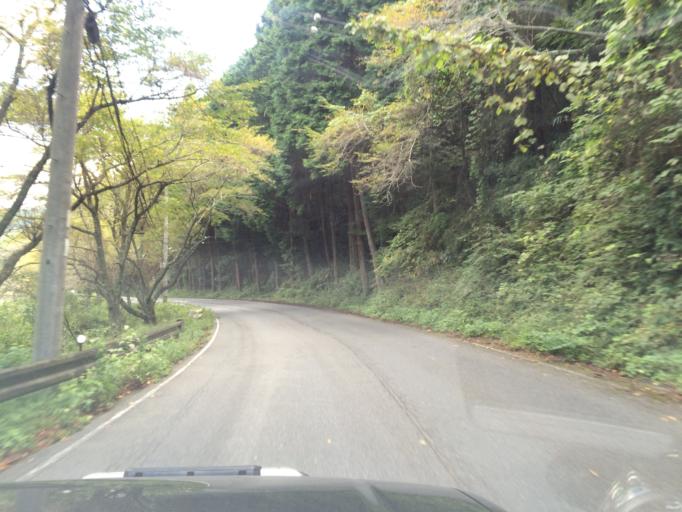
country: JP
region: Mie
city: Nabari
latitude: 34.6773
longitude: 135.9705
